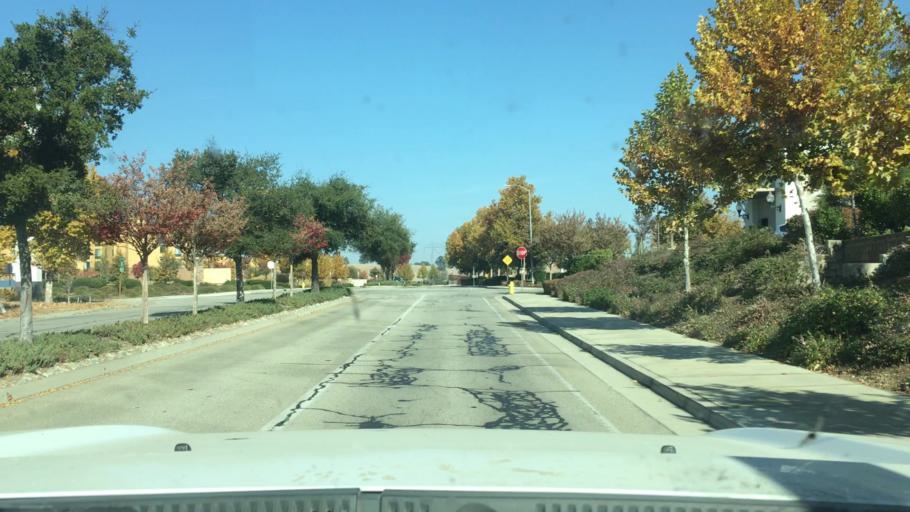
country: US
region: California
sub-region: San Luis Obispo County
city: Templeton
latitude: 35.5258
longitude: -120.7031
